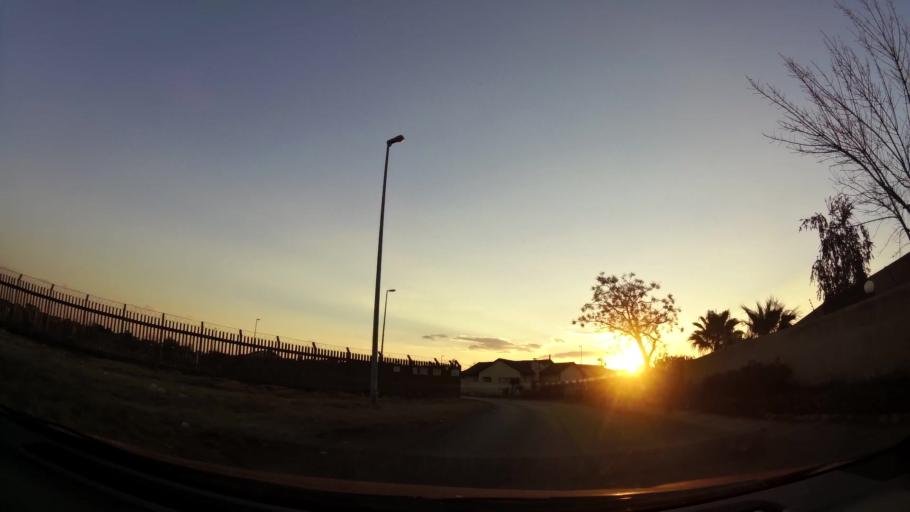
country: ZA
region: Gauteng
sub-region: City of Johannesburg Metropolitan Municipality
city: Soweto
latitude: -26.2264
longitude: 27.8450
